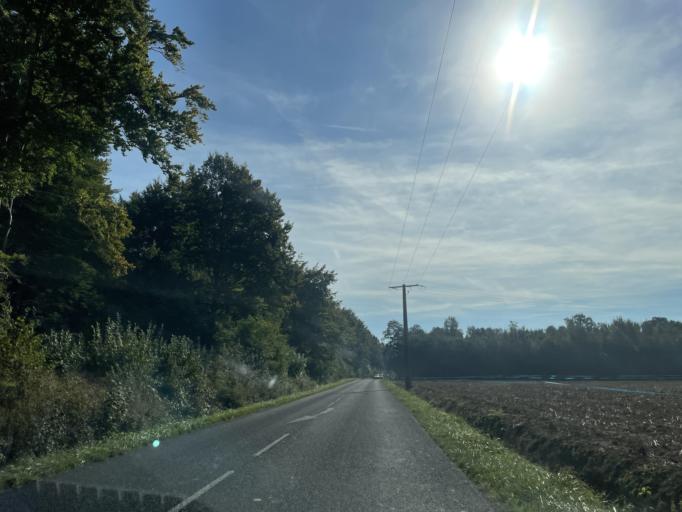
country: FR
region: Ile-de-France
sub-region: Departement de Seine-et-Marne
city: Saint-Jean-les-Deux-Jumeaux
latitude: 48.9211
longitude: 3.0071
